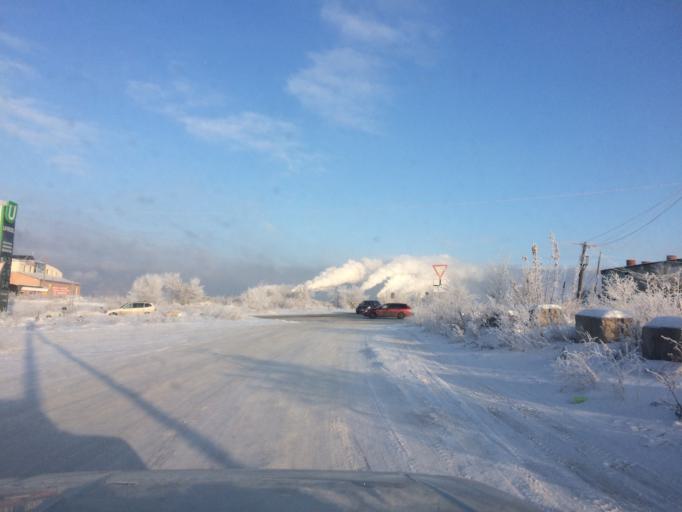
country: RU
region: Chelyabinsk
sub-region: Gorod Magnitogorsk
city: Magnitogorsk
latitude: 53.3946
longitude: 59.0846
